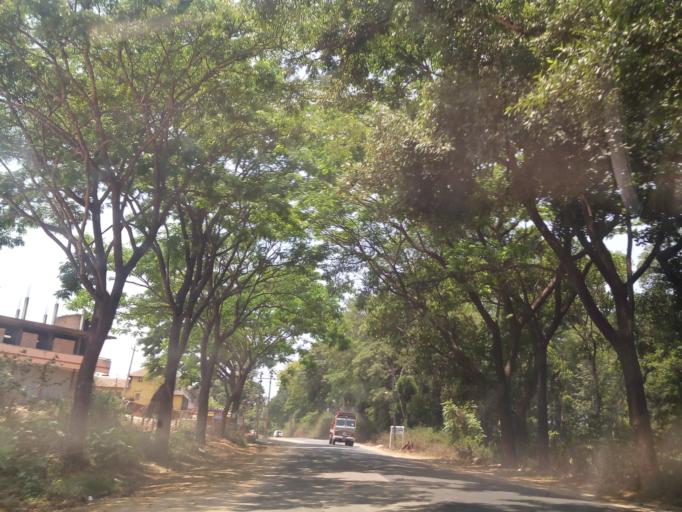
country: IN
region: Karnataka
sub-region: Hassan
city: Sakleshpur
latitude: 12.9492
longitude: 75.8070
